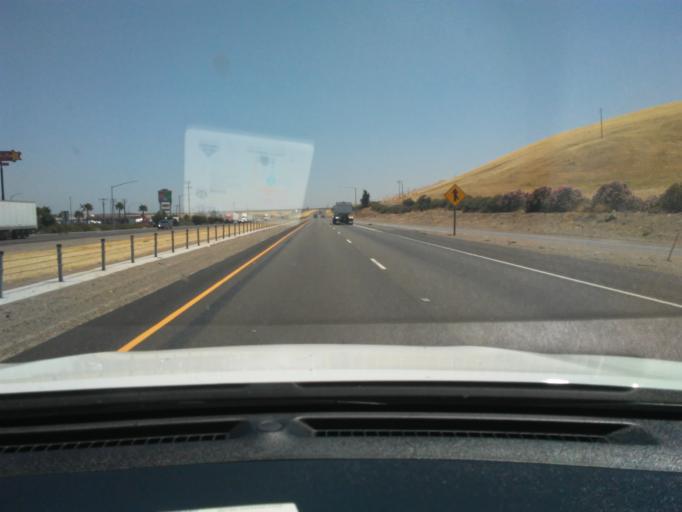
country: US
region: California
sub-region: Stanislaus County
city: Patterson
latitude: 37.5392
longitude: -121.2667
